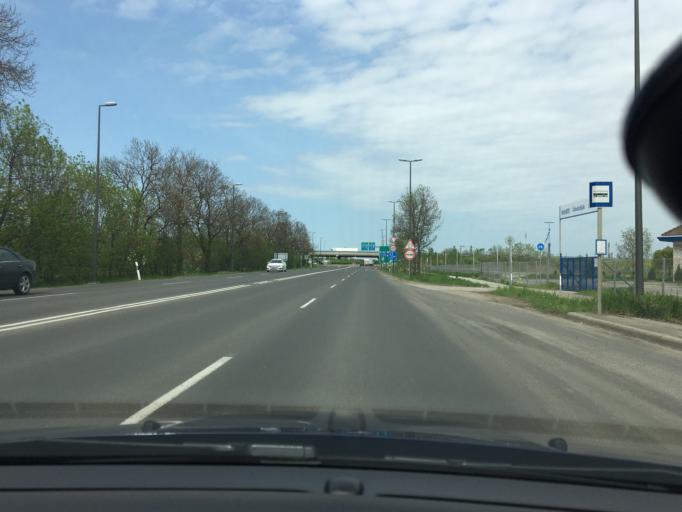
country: HU
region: Csongrad
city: Szeged
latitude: 46.2920
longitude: 20.1750
